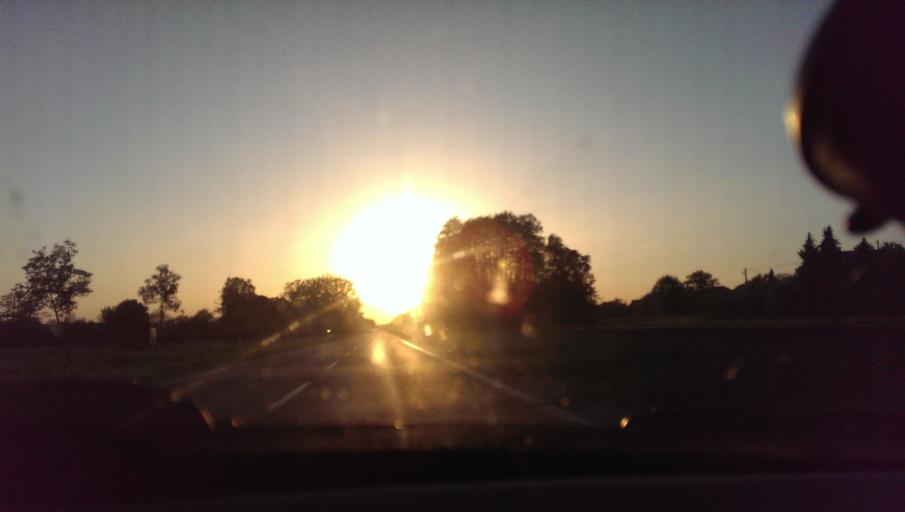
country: CZ
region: Zlin
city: Zasova
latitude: 49.4663
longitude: 18.0492
